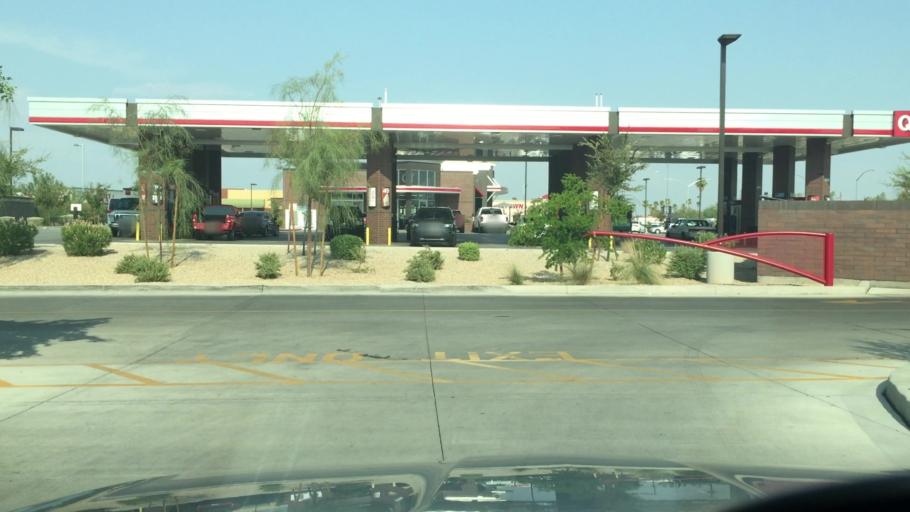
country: US
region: Arizona
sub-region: Maricopa County
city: Tempe
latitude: 33.4082
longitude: -111.8764
